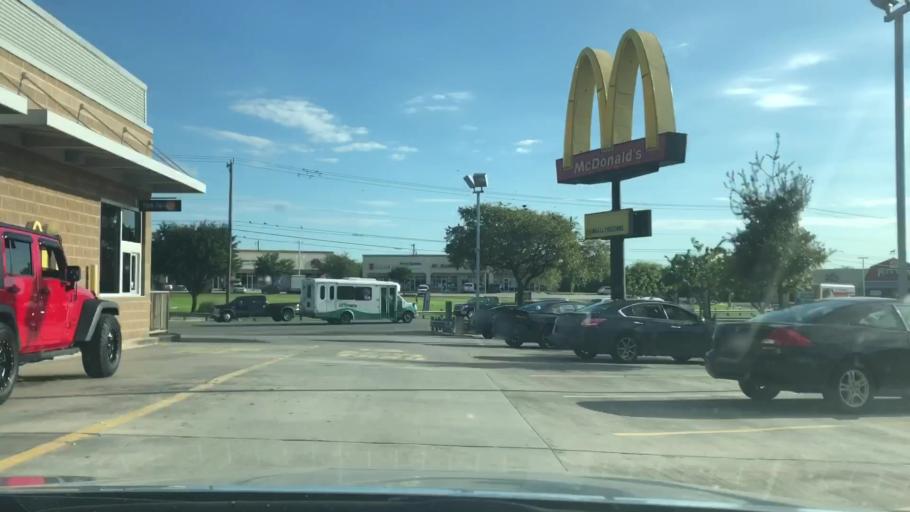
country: US
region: Texas
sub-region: Bexar County
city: Kirby
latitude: 29.4801
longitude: -98.3627
